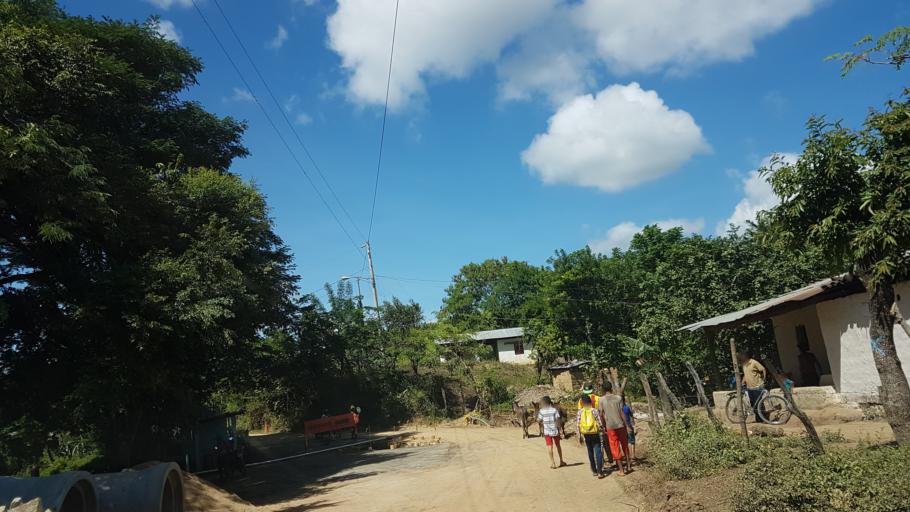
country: HN
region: El Paraiso
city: Santa Cruz
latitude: 13.7327
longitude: -86.6858
